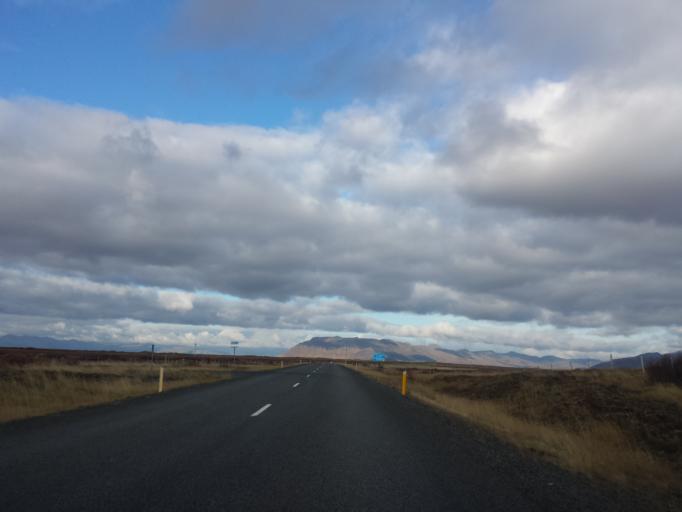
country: IS
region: West
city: Borgarnes
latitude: 64.6521
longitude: -22.0645
